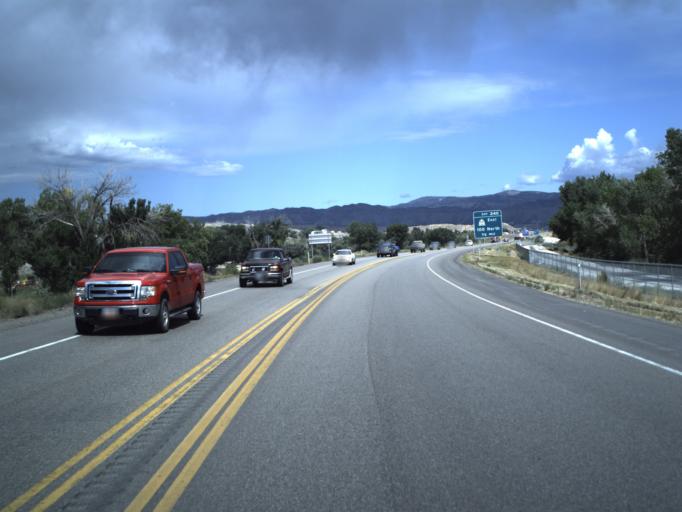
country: US
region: Utah
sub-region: Carbon County
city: Price
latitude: 39.5913
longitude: -110.8194
